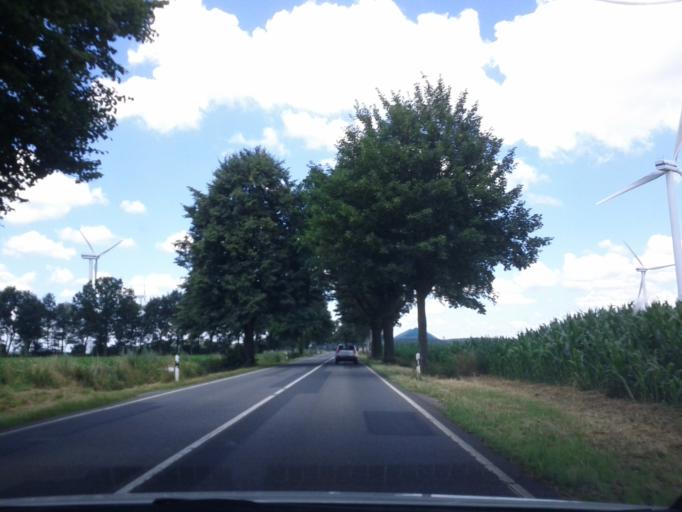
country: DE
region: Lower Saxony
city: Apensen
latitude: 53.4555
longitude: 9.6030
